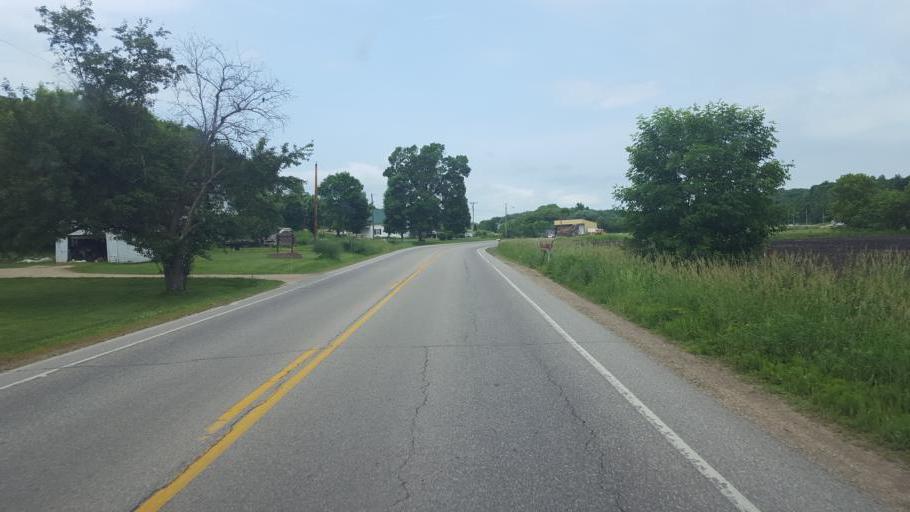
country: US
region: Wisconsin
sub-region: Monroe County
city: Cashton
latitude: 43.7236
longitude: -90.6012
